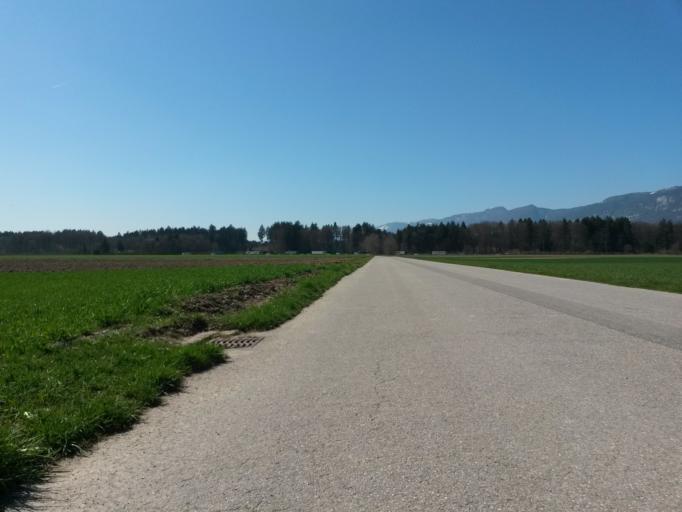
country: CH
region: Solothurn
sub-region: Bezirk Wasseramt
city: Deitingen
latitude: 47.2144
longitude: 7.6099
